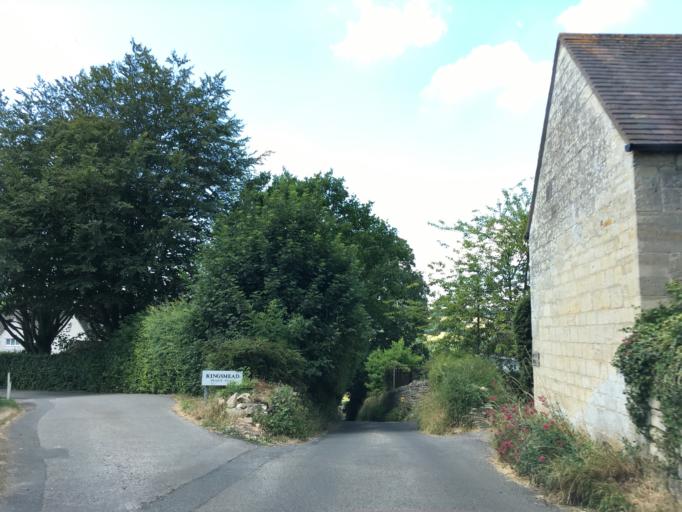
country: GB
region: England
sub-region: Gloucestershire
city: Painswick
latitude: 51.7864
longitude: -2.2001
